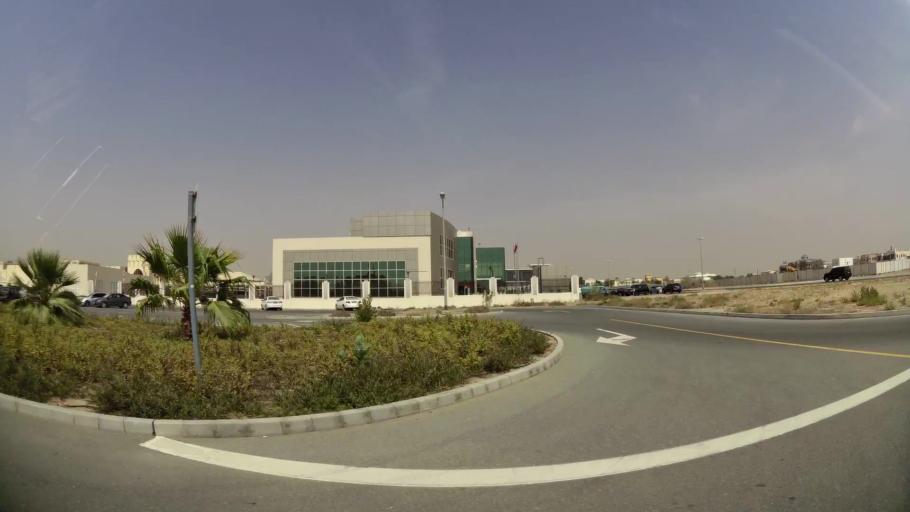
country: AE
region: Ash Shariqah
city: Sharjah
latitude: 25.2448
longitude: 55.4500
